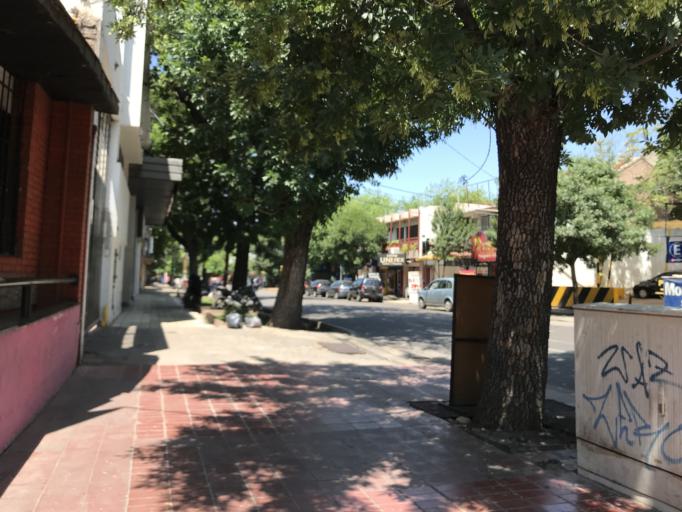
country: AR
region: Mendoza
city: Mendoza
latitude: -32.8843
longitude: -68.8425
